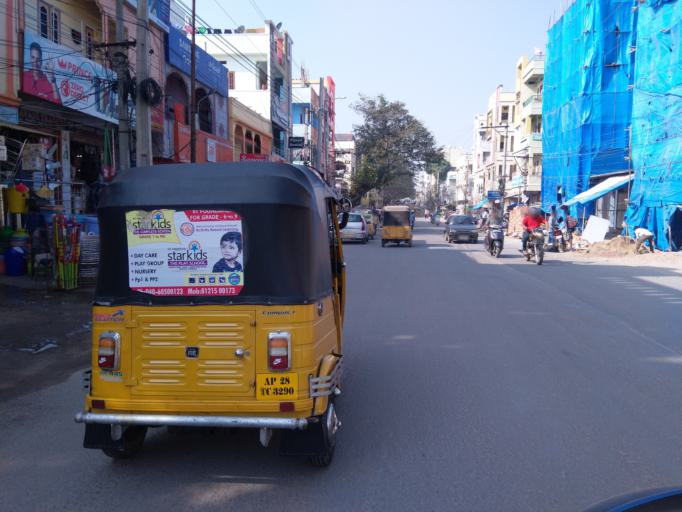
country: IN
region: Telangana
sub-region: Rangareddi
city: Kukatpalli
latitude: 17.5024
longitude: 78.4197
